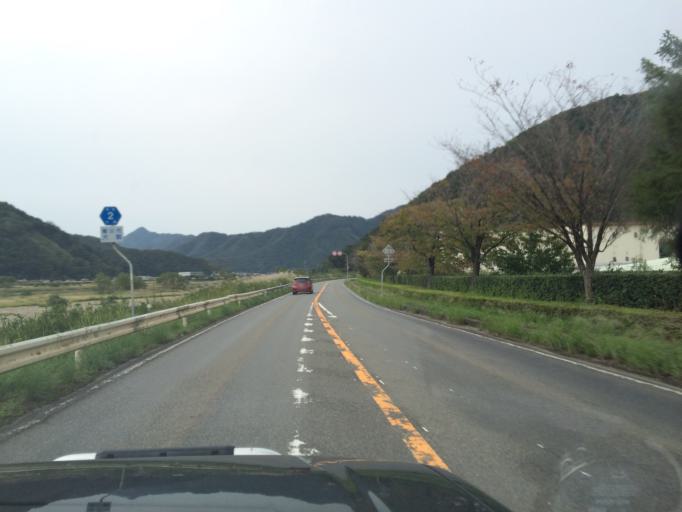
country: JP
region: Hyogo
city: Toyooka
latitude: 35.3930
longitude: 134.7944
